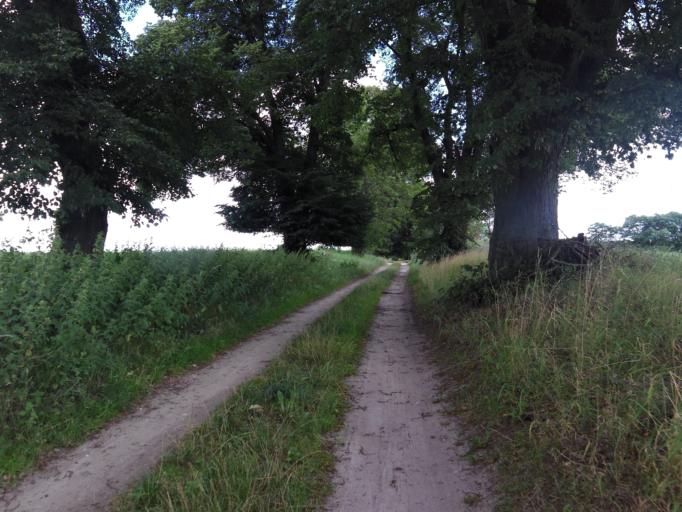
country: DE
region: Brandenburg
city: Lychen
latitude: 53.2322
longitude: 13.3444
